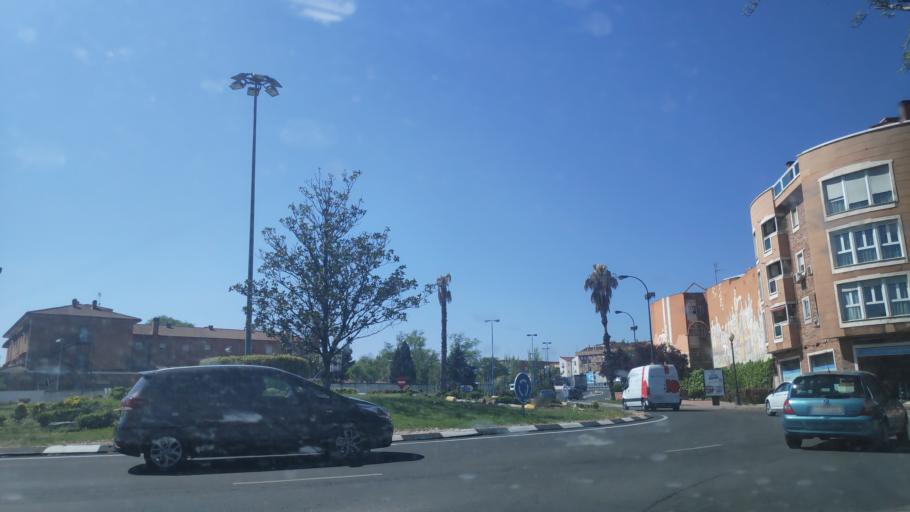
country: ES
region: Madrid
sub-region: Provincia de Madrid
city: Getafe
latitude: 40.3047
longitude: -3.7249
